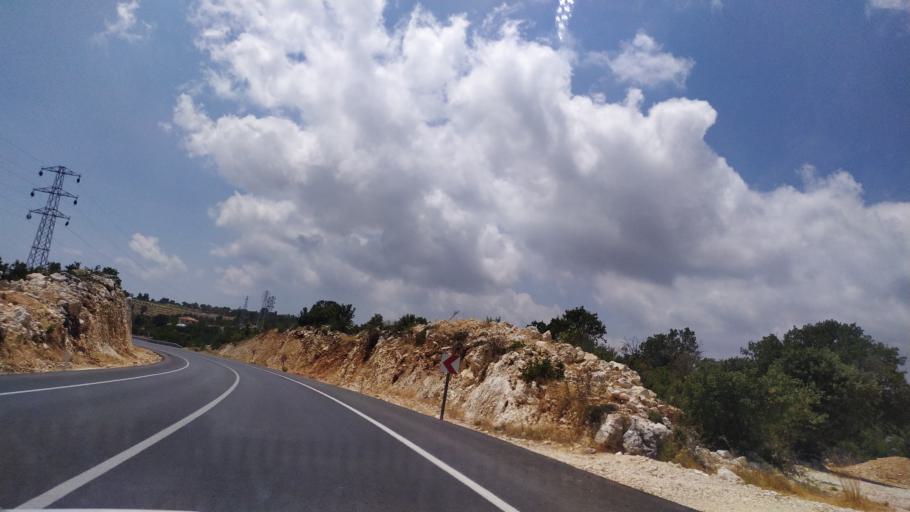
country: TR
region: Mersin
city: Gulnar
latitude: 36.2641
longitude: 33.3659
